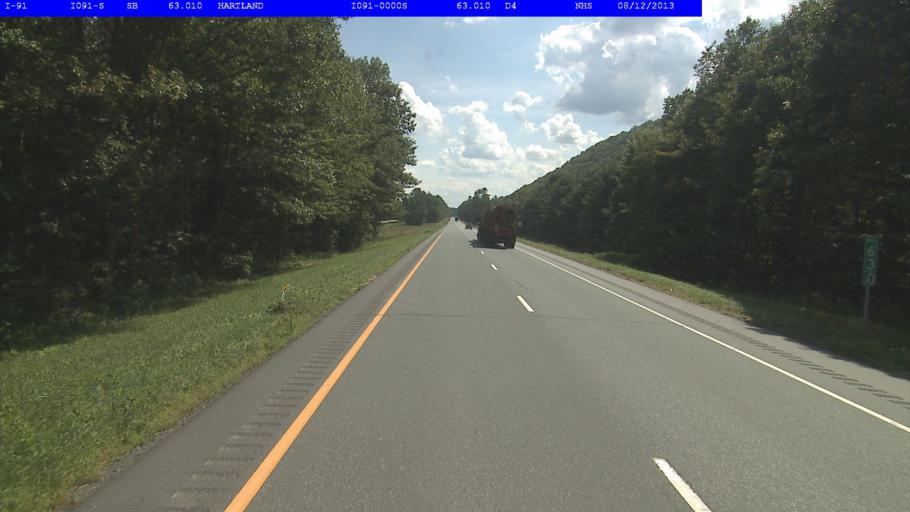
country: US
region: Vermont
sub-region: Windsor County
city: Windsor
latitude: 43.5609
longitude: -72.3855
